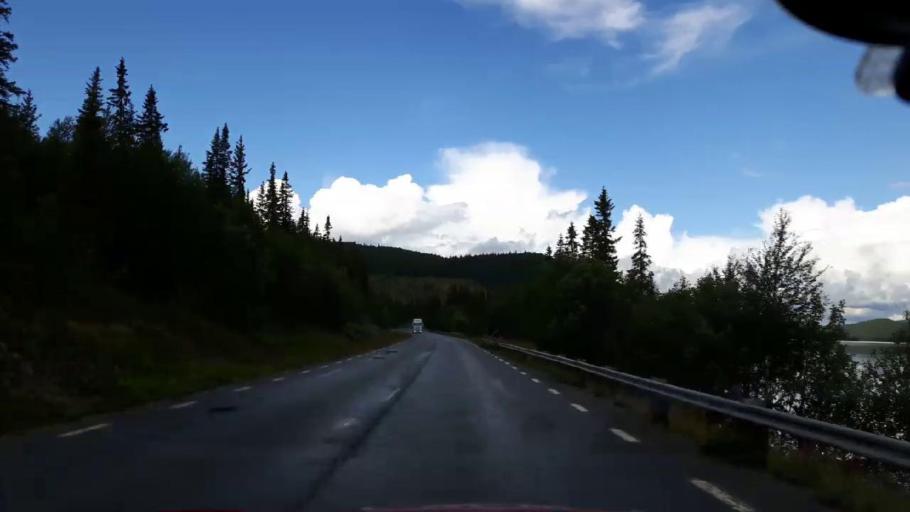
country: SE
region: Vaesterbotten
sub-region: Vilhelmina Kommun
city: Sjoberg
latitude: 64.9950
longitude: 15.2178
